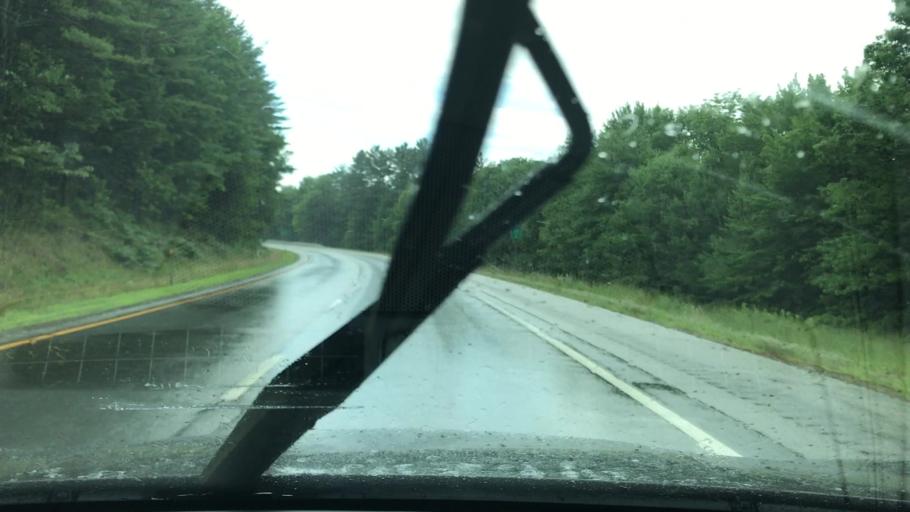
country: US
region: New Hampshire
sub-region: Grafton County
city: Littleton
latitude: 44.3019
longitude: -71.7756
